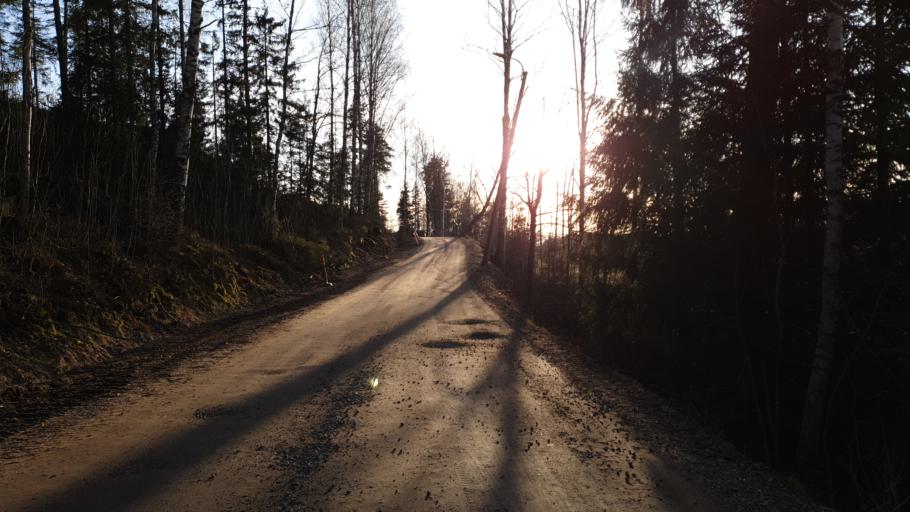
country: FI
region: Uusimaa
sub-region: Helsinki
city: Nurmijaervi
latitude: 60.3423
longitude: 24.8609
